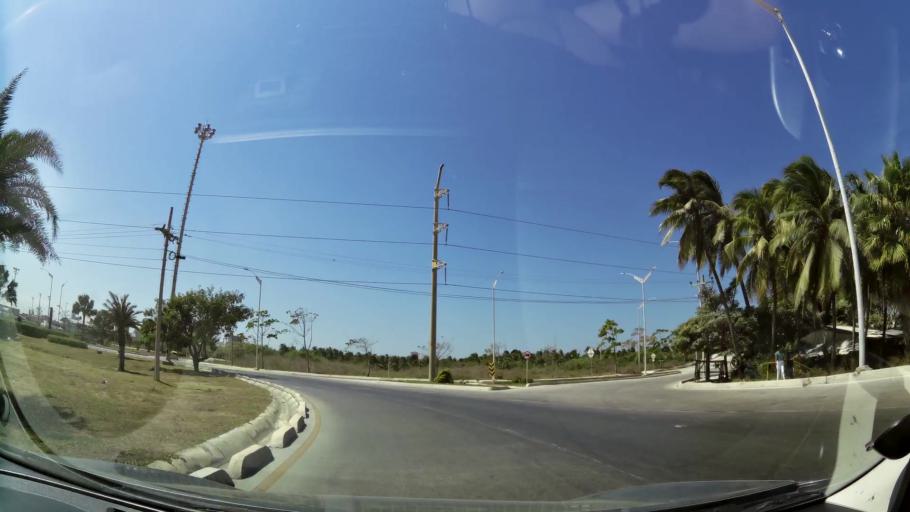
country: CO
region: Atlantico
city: Barranquilla
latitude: 10.9878
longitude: -74.7703
